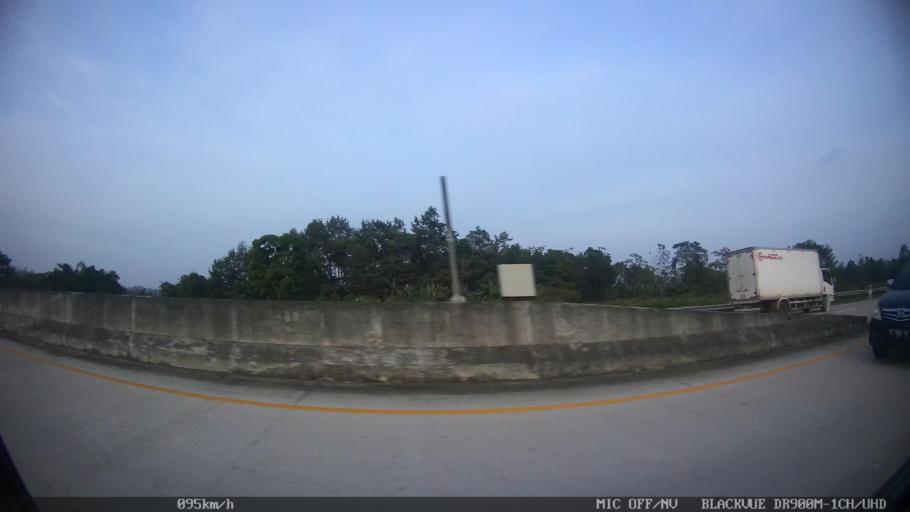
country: ID
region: Lampung
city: Penengahan
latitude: -5.7654
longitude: 105.7146
